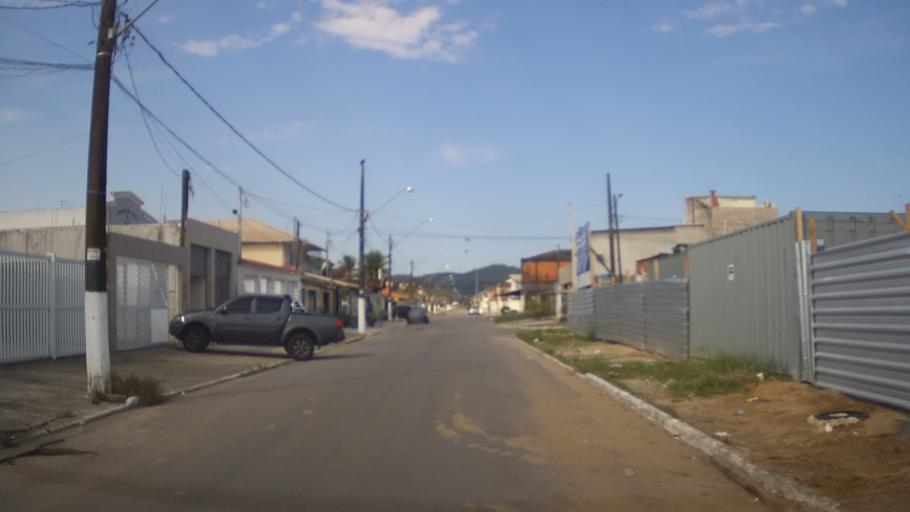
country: BR
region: Sao Paulo
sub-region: Praia Grande
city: Praia Grande
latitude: -23.9987
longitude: -46.4309
